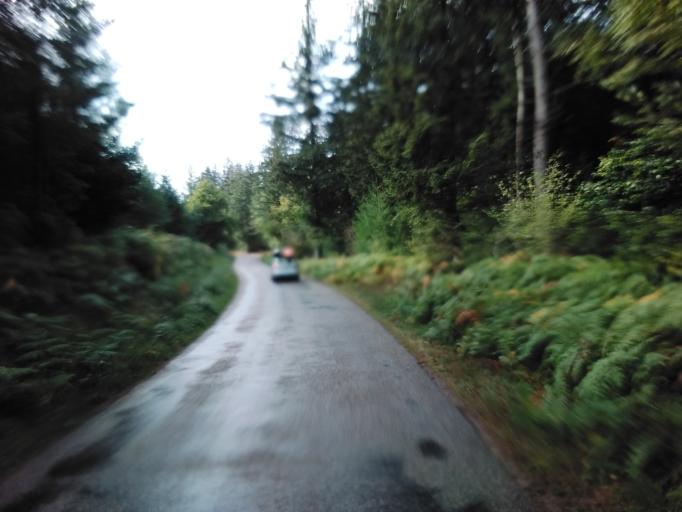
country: FR
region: Bourgogne
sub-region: Departement de la Nievre
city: Lormes
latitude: 47.2984
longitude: 3.8746
